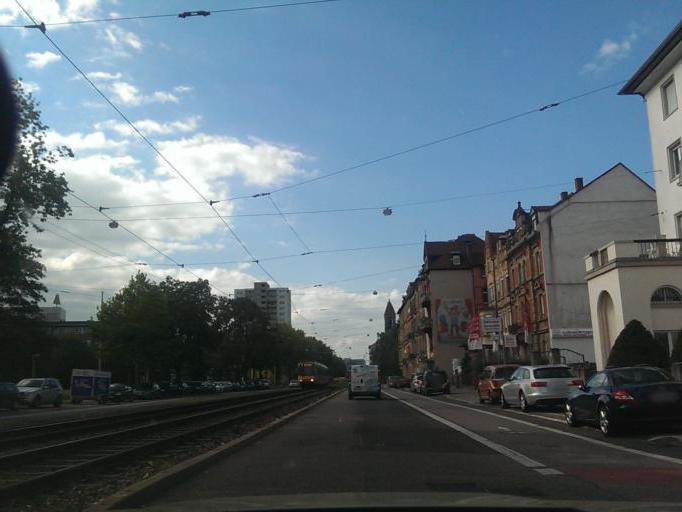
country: DE
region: Baden-Wuerttemberg
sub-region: Karlsruhe Region
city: Karlsruhe
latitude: 49.0068
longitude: 8.4291
